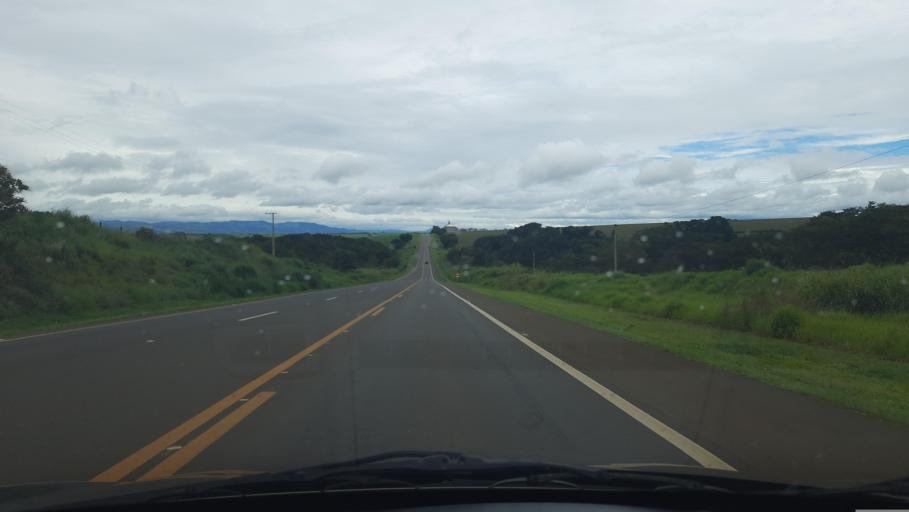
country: BR
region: Sao Paulo
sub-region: Casa Branca
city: Casa Branca
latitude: -21.7920
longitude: -47.0352
